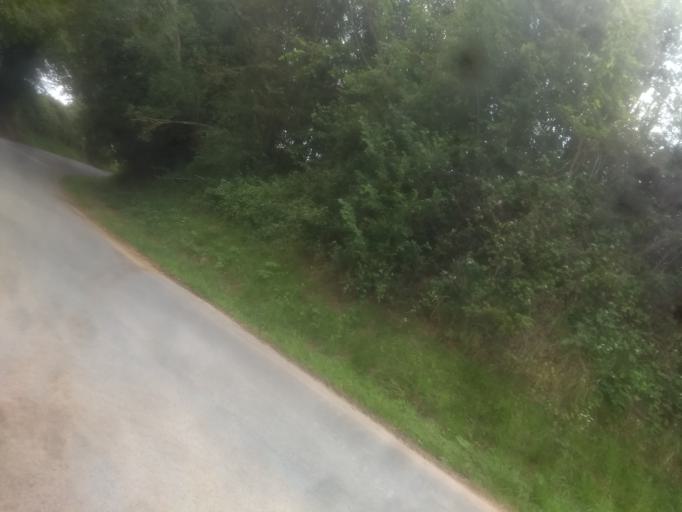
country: FR
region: Nord-Pas-de-Calais
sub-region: Departement du Pas-de-Calais
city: Duisans
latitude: 50.3127
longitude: 2.6484
